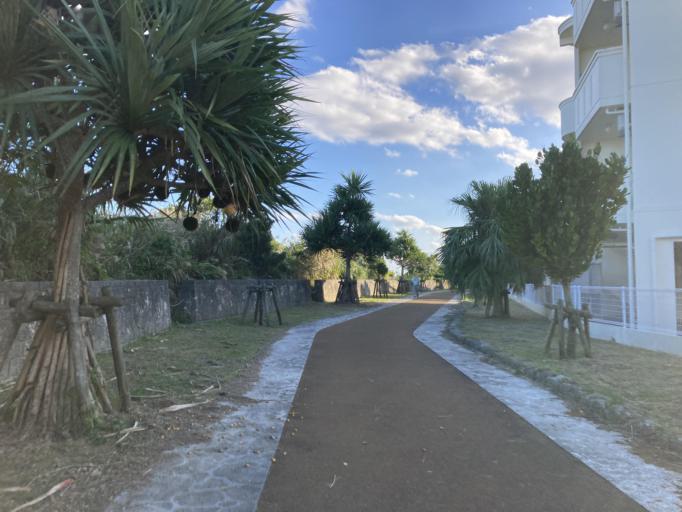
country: JP
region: Okinawa
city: Ginowan
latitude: 26.2551
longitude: 127.7770
